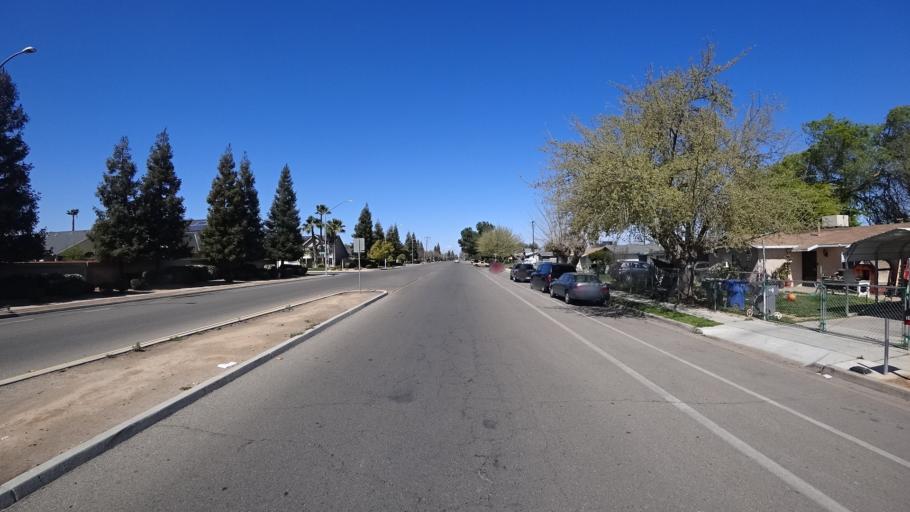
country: US
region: California
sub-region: Fresno County
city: West Park
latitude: 36.7811
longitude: -119.8623
